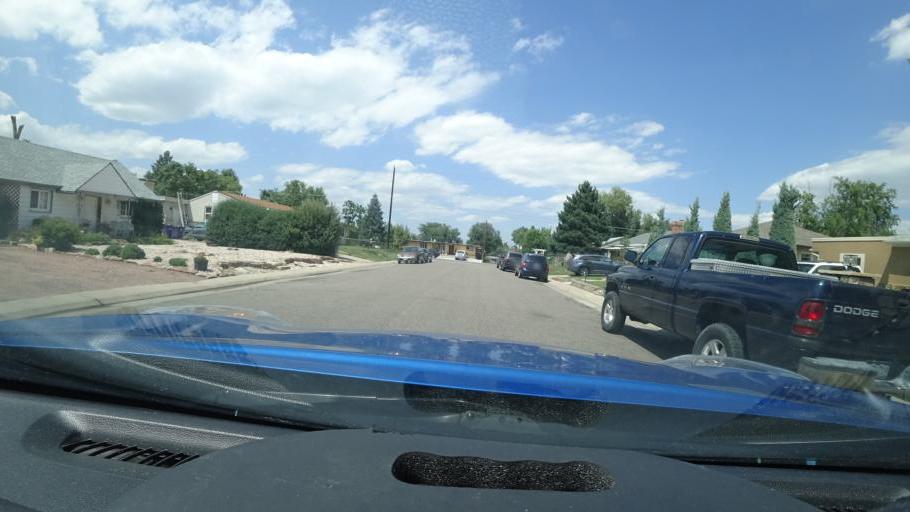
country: US
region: Colorado
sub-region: Jefferson County
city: Lakewood
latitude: 39.7036
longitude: -105.0473
